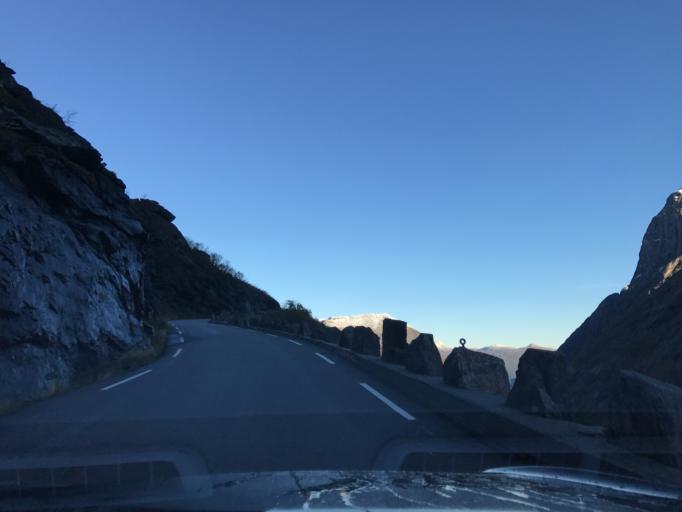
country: NO
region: More og Romsdal
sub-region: Rauma
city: Andalsnes
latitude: 62.4573
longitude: 7.6698
